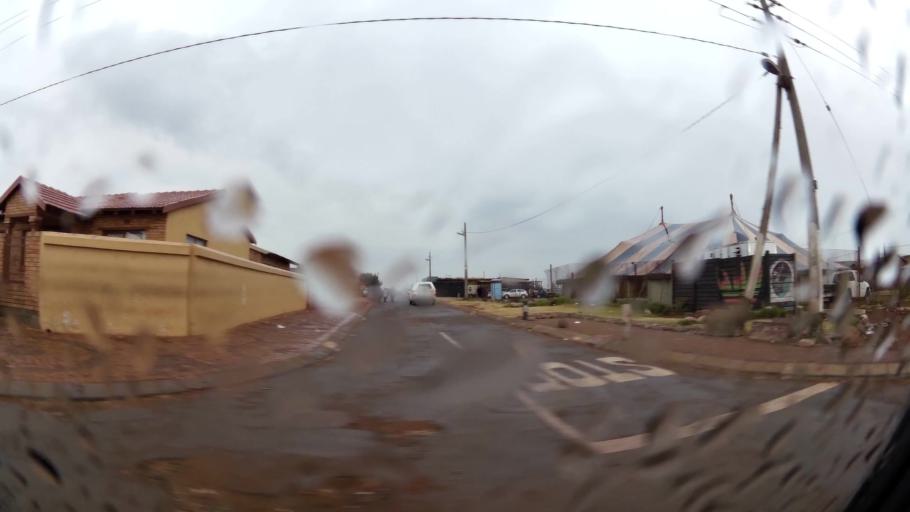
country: ZA
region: Gauteng
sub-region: West Rand District Municipality
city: Randfontein
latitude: -26.1744
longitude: 27.7867
